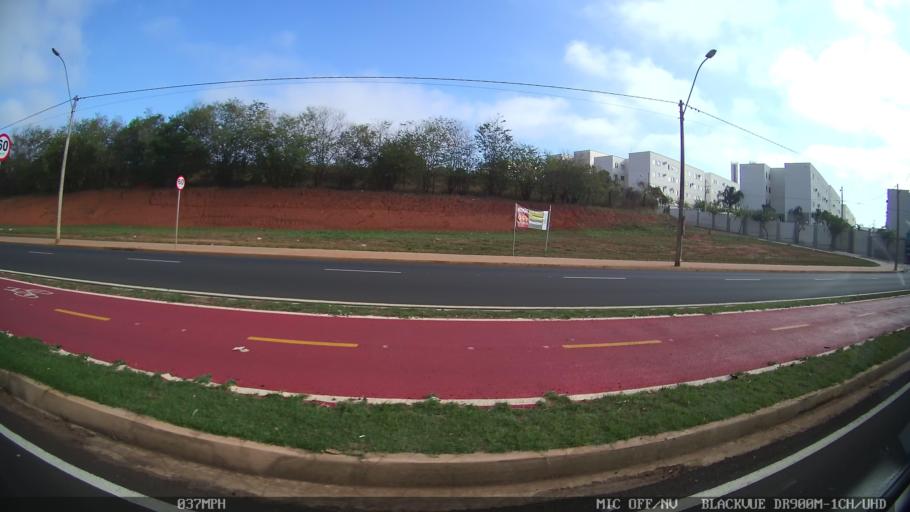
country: BR
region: Sao Paulo
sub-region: Sao Jose Do Rio Preto
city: Sao Jose do Rio Preto
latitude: -20.8082
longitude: -49.4296
